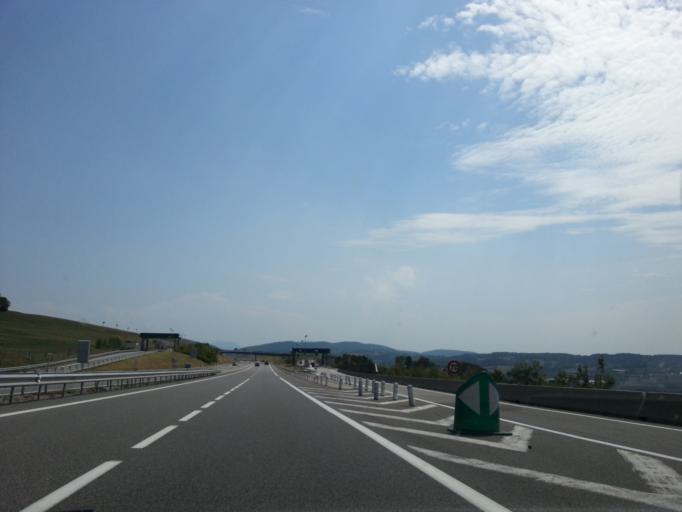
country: FR
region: Rhone-Alpes
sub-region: Departement de la Haute-Savoie
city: Cruseilles
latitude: 46.0524
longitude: 6.0803
